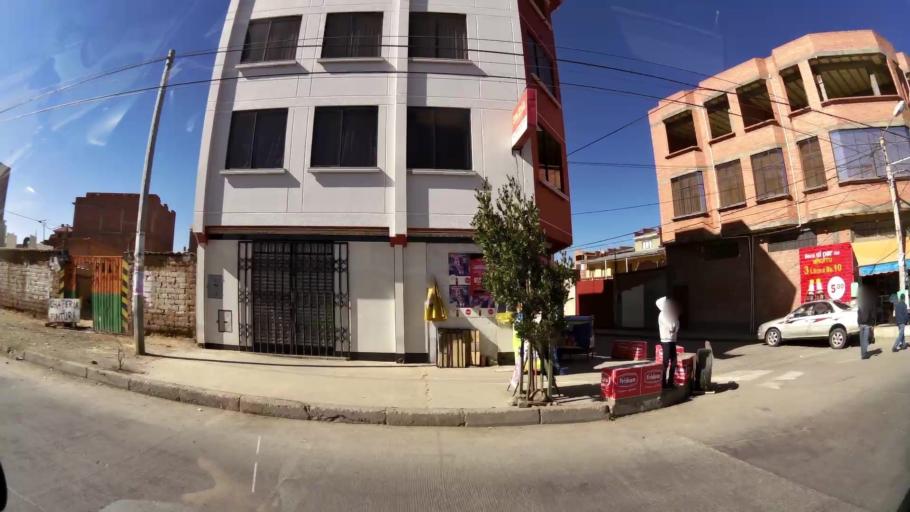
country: BO
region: La Paz
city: La Paz
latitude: -16.5240
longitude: -68.1973
